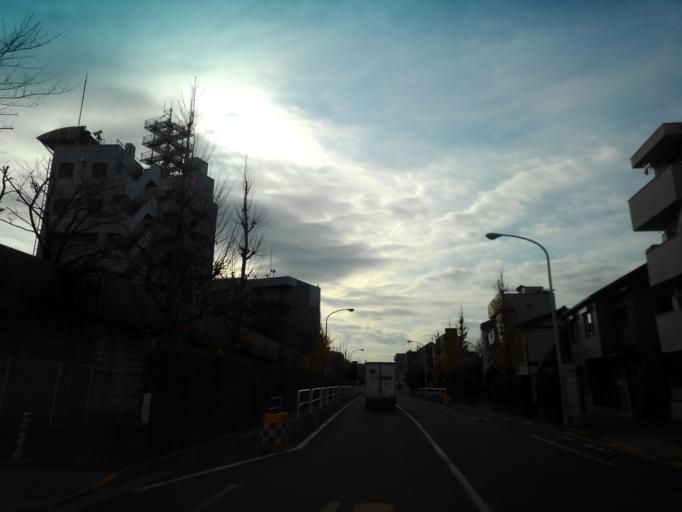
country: JP
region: Tokyo
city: Tokyo
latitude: 35.6724
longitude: 139.6715
